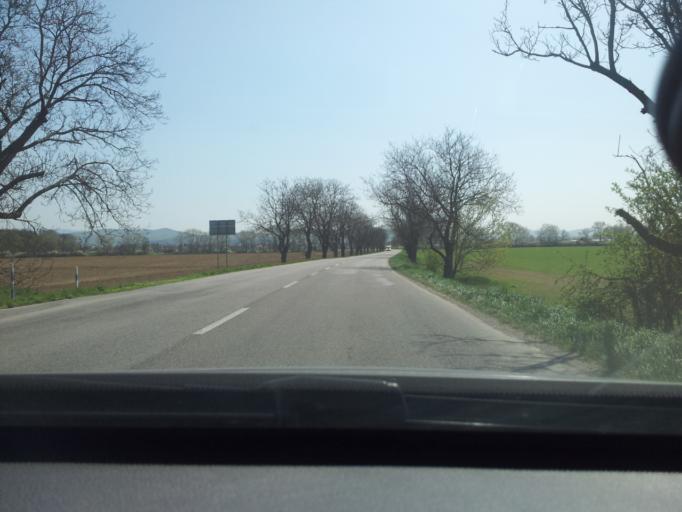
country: SK
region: Nitriansky
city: Banovce nad Bebravou
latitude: 48.6161
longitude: 18.2530
